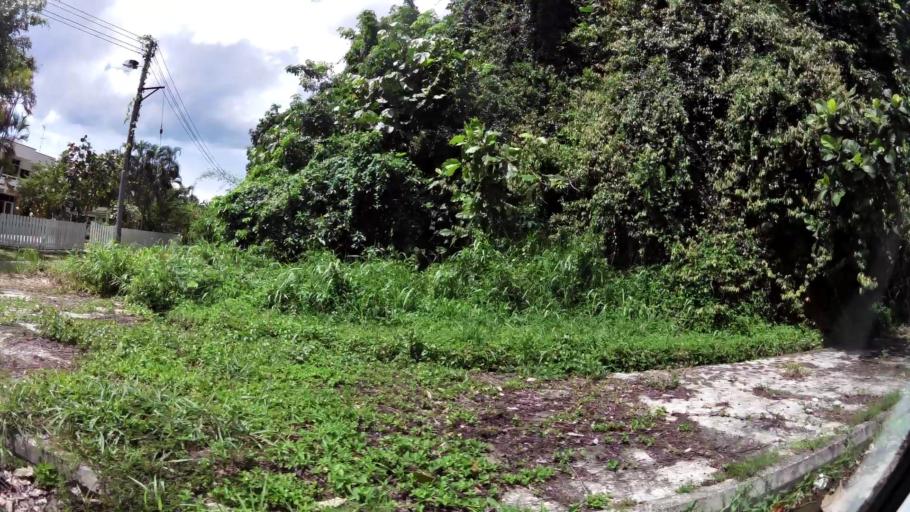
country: BN
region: Brunei and Muara
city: Bandar Seri Begawan
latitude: 4.9432
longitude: 114.9653
